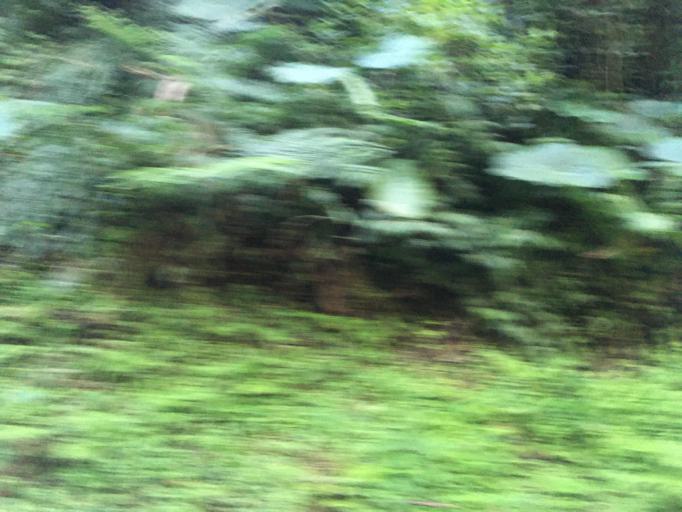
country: TW
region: Taiwan
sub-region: Yilan
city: Yilan
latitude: 24.7578
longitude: 121.6135
